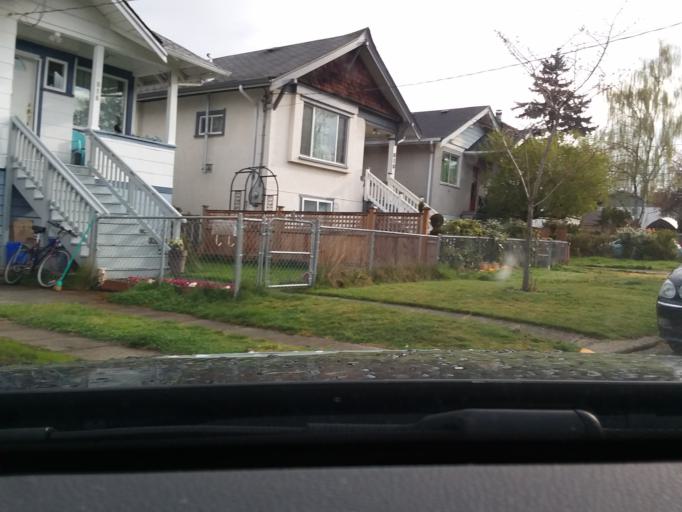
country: CA
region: British Columbia
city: Victoria
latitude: 48.4382
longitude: -123.3949
